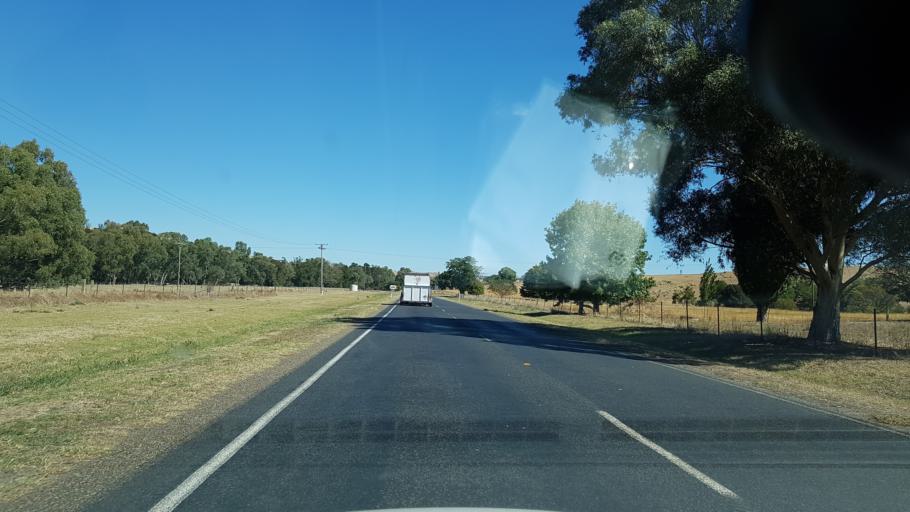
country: AU
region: New South Wales
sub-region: Gundagai
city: Gundagai
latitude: -34.8211
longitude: 148.3519
